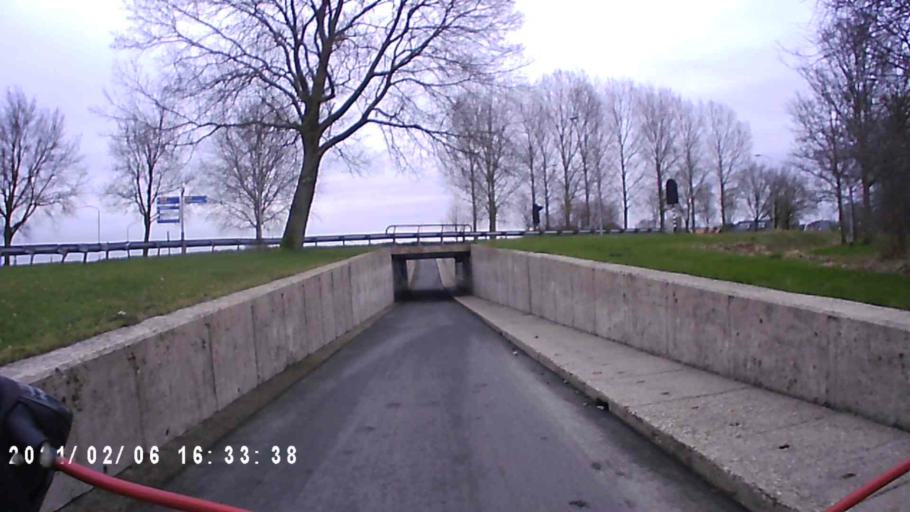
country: NL
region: Groningen
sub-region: Gemeente Bedum
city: Bedum
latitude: 53.4124
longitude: 6.6941
